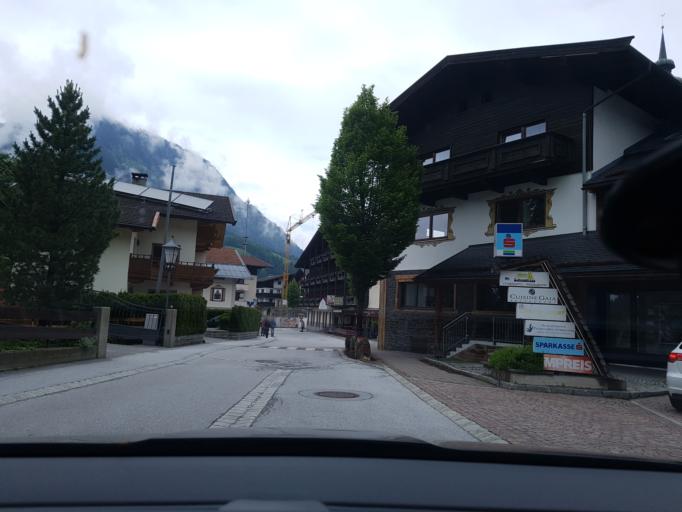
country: AT
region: Tyrol
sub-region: Politischer Bezirk Kufstein
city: Soll
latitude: 47.5026
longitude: 12.1927
